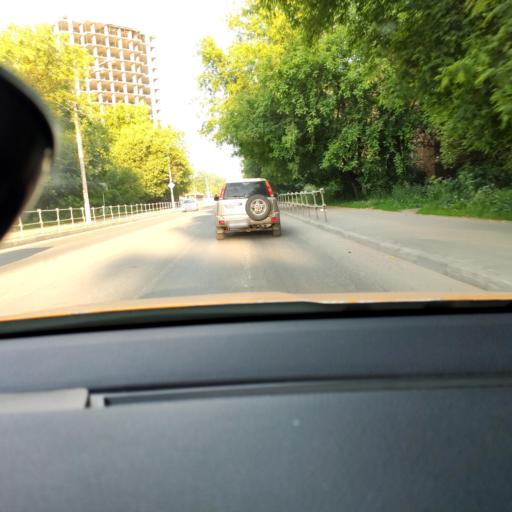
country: RU
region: Moskovskaya
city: Zagoryanskiy
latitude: 55.9252
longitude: 37.9632
